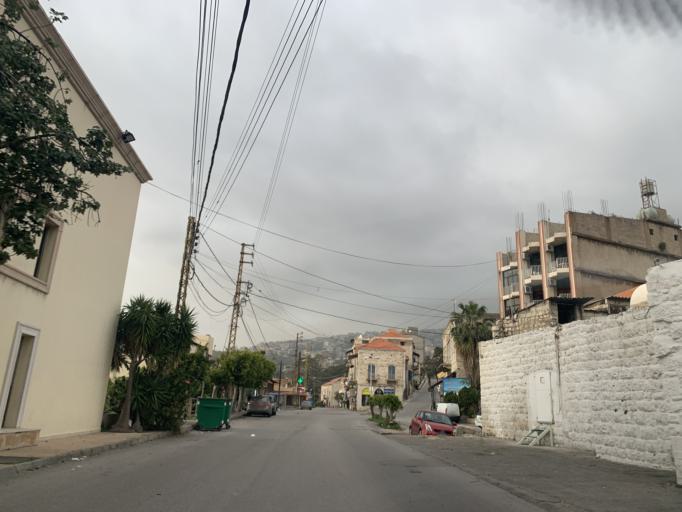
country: LB
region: Mont-Liban
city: Djounie
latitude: 34.0052
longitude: 35.6451
